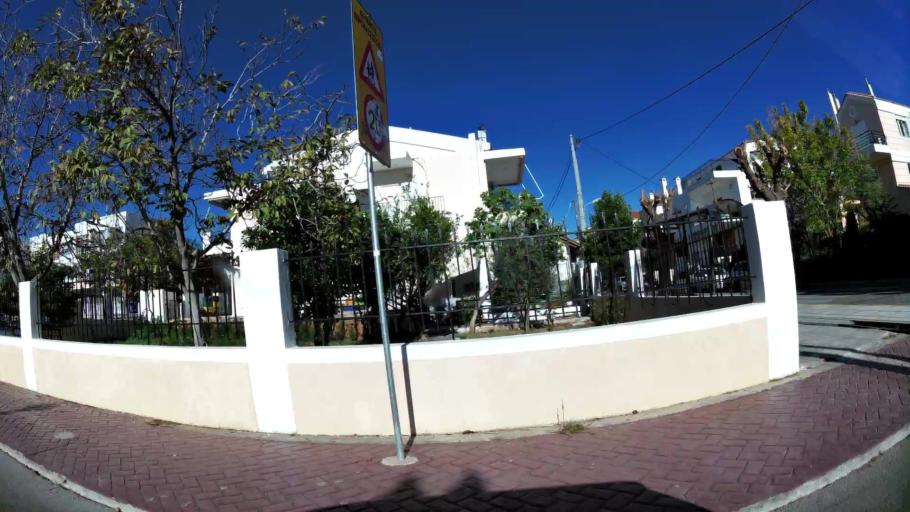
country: GR
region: Attica
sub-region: Nomarchia Athinas
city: Melissia
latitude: 38.0400
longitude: 23.8399
